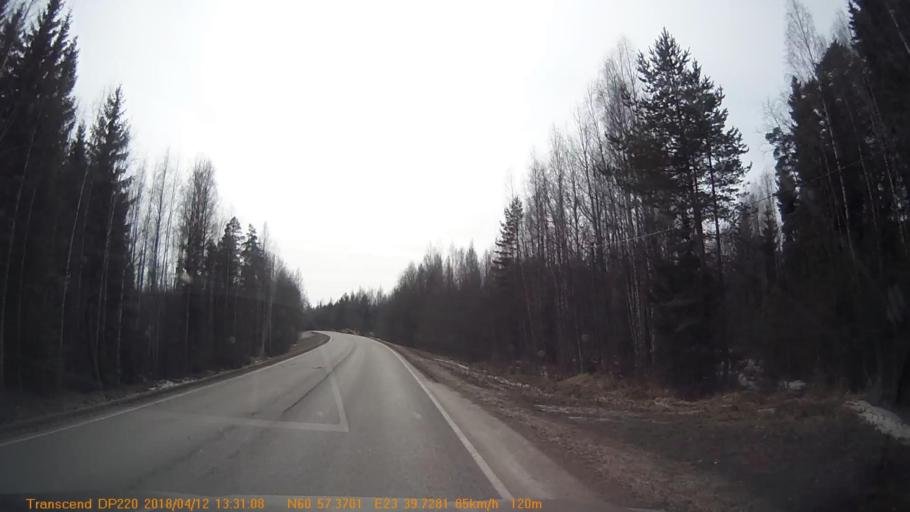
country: FI
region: Haeme
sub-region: Forssa
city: Forssa
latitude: 60.9561
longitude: 23.6621
